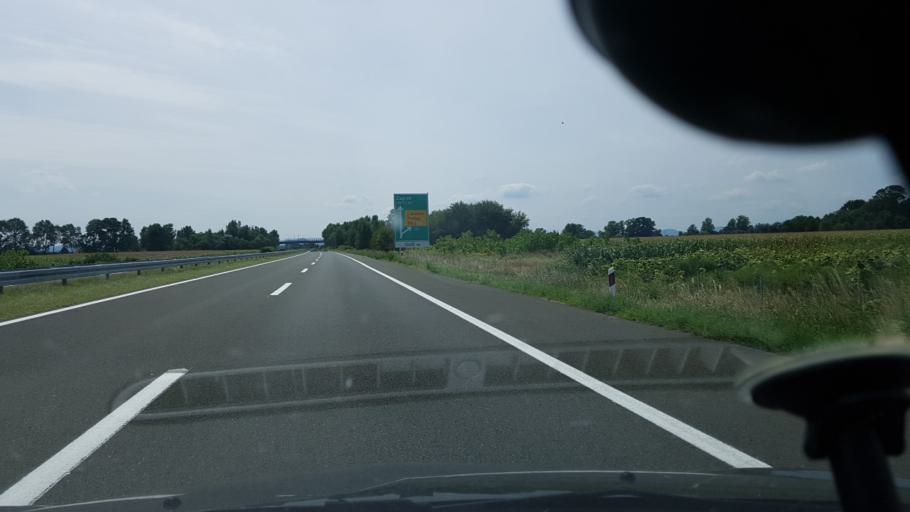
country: HR
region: Medimurska
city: Mala Subotica
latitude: 46.3613
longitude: 16.5396
